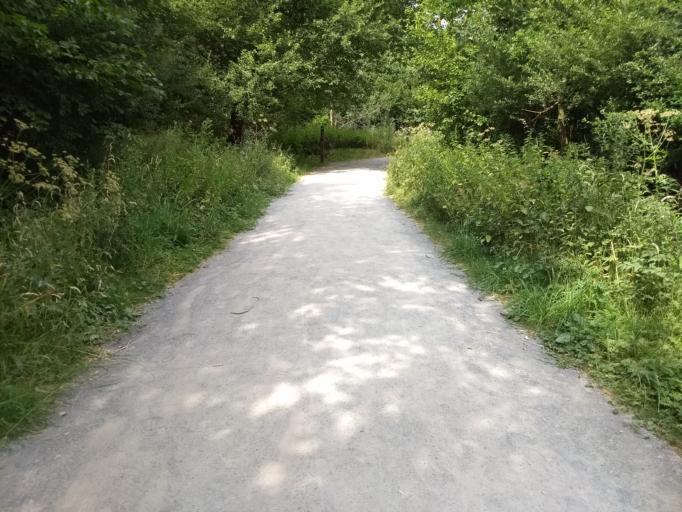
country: GB
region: England
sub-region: Northamptonshire
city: Hartwell
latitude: 52.1607
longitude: -0.8375
